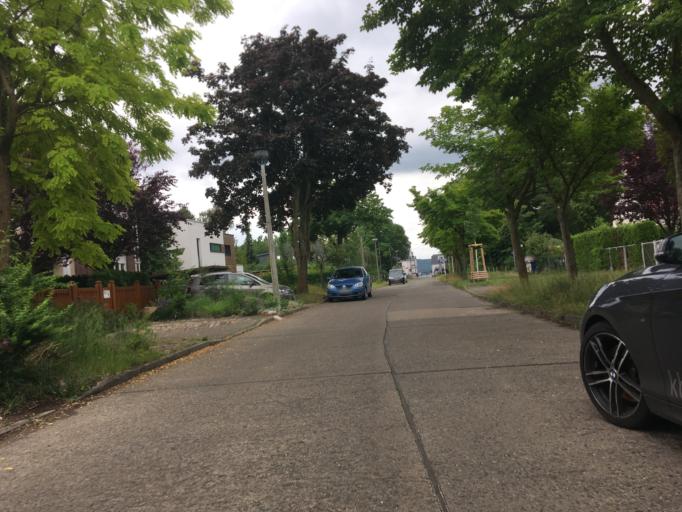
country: DE
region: Berlin
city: Friedrichshagen
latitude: 52.4493
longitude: 13.6403
